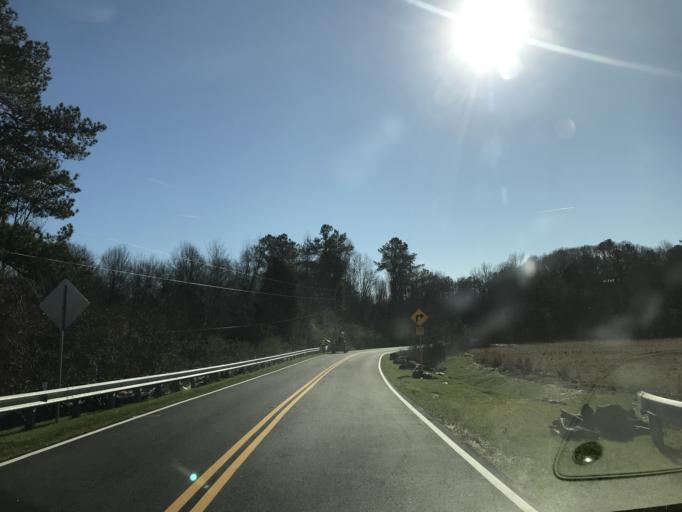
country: US
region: Georgia
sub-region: Paulding County
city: Dallas
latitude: 33.9971
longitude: -84.8951
